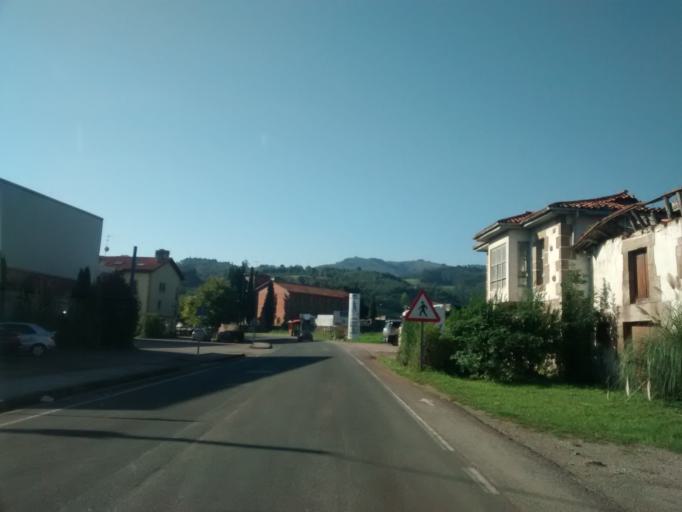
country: ES
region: Cantabria
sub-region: Provincia de Cantabria
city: Cartes
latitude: 43.3256
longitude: -4.0714
